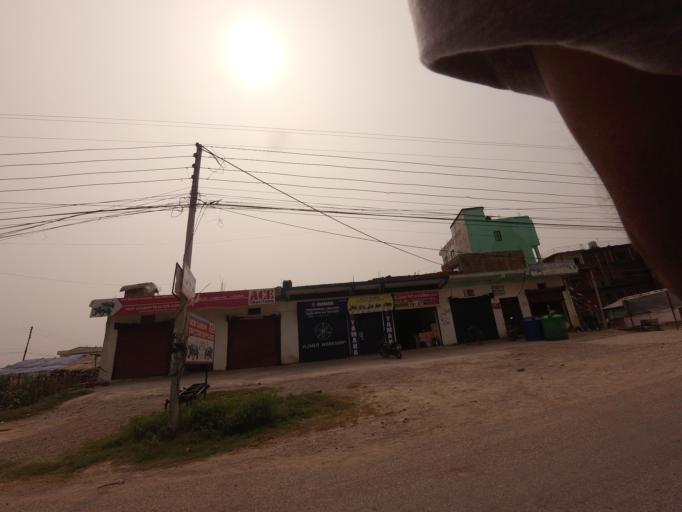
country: IN
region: Uttar Pradesh
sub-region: Maharajganj
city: Nautanwa
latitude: 27.4929
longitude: 83.2843
